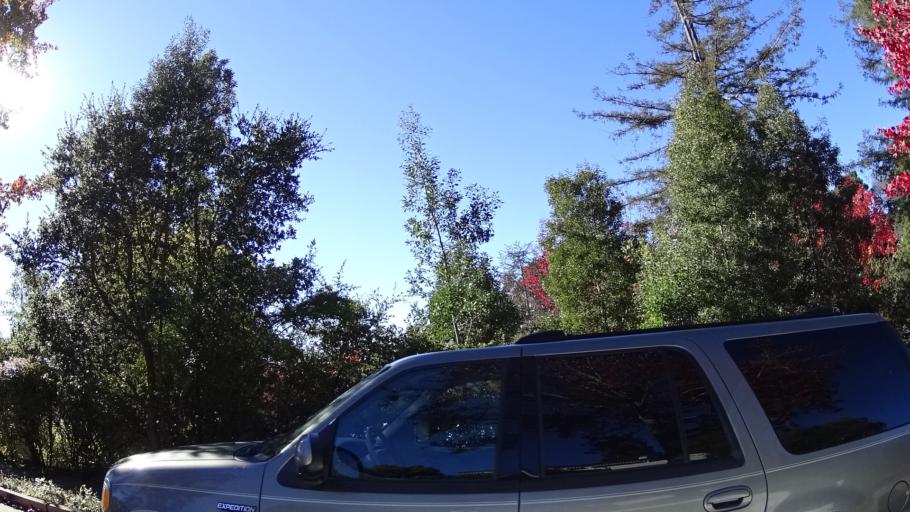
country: US
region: California
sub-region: Alameda County
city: Piedmont
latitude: 37.8195
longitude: -122.2163
